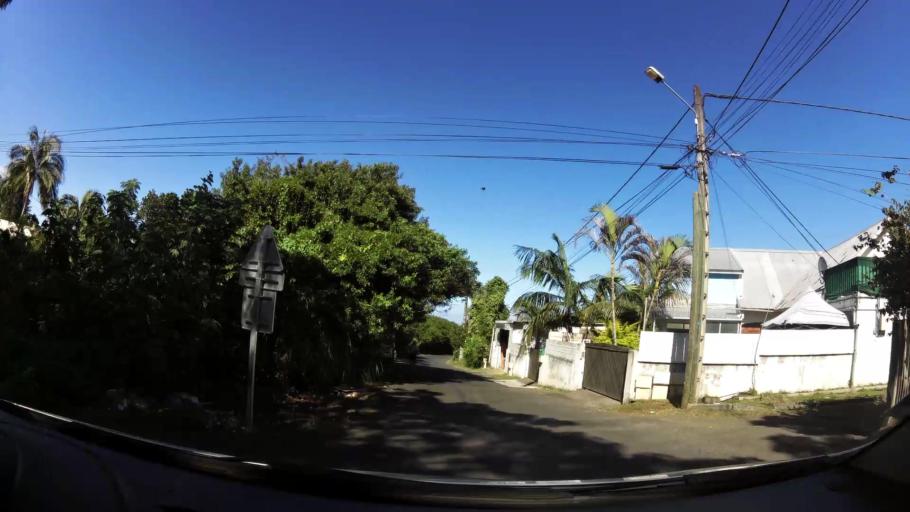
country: RE
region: Reunion
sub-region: Reunion
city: Le Tampon
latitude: -21.2652
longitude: 55.5031
